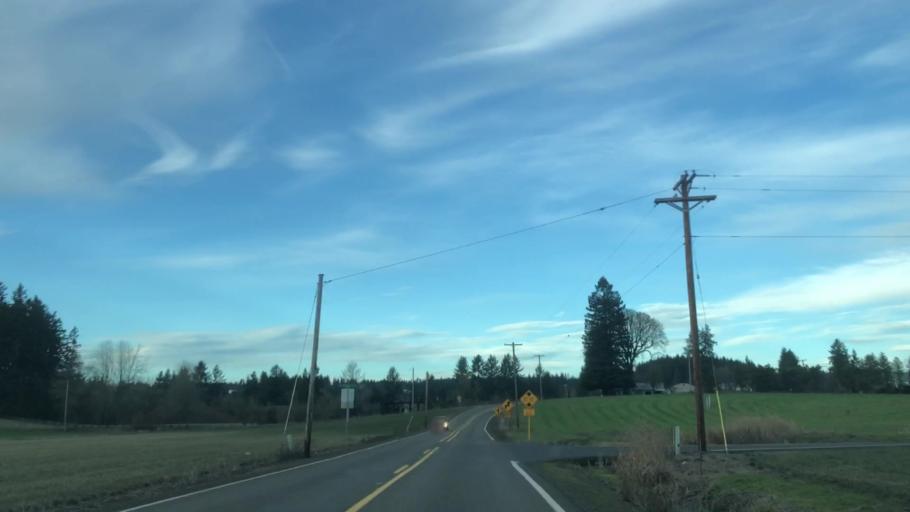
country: US
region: Oregon
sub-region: Washington County
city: Rockcreek
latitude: 45.5918
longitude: -122.9193
